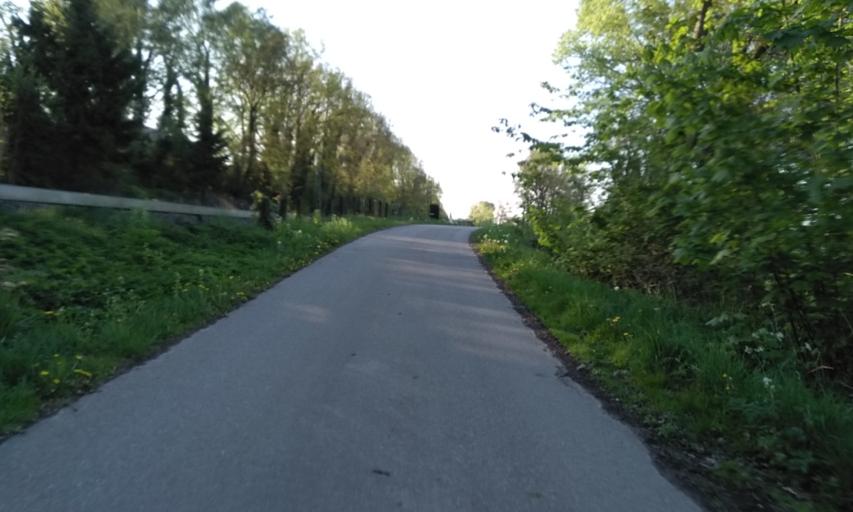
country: DE
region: Lower Saxony
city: Dollern
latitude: 53.5400
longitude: 9.5617
